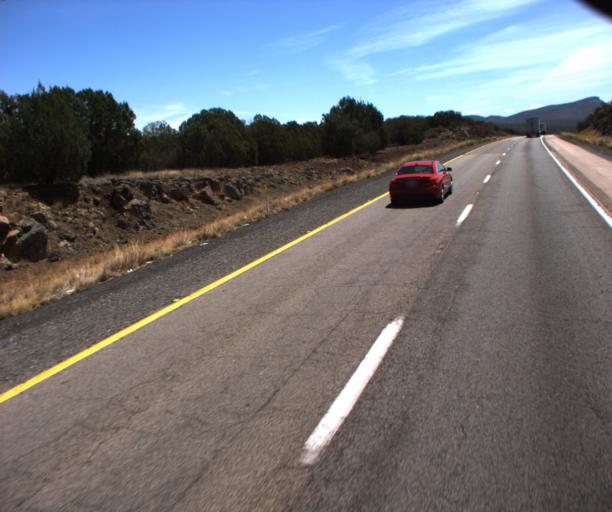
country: US
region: Arizona
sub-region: Mohave County
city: Peach Springs
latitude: 35.1904
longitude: -113.3307
